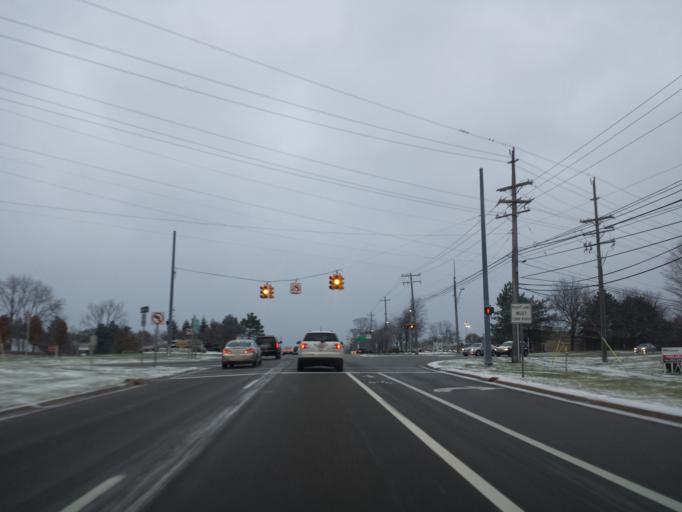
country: US
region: Michigan
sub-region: Oakland County
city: Franklin
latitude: 42.5074
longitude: -83.3207
